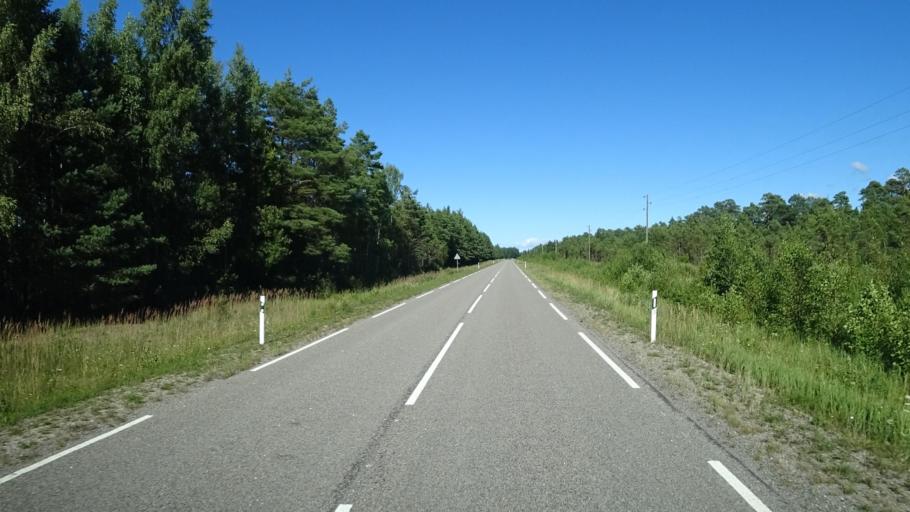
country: LV
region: Dundaga
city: Dundaga
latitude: 57.6946
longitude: 22.3977
